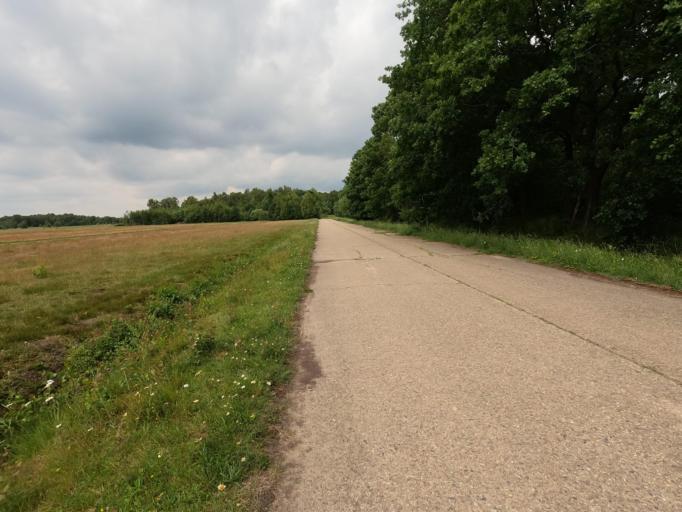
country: BE
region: Flanders
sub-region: Provincie Antwerpen
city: Brasschaat
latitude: 51.3404
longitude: 4.5078
